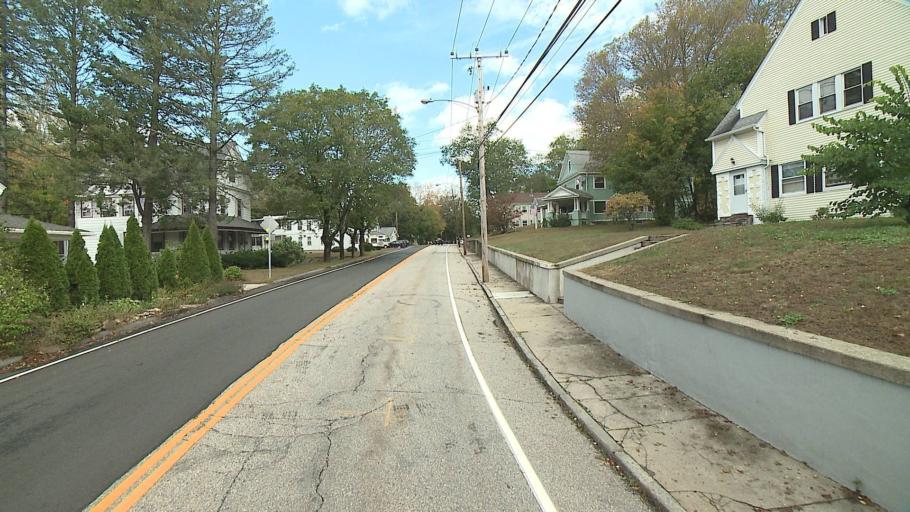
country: US
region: Connecticut
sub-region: Windham County
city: Putnam
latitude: 41.9256
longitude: -71.9001
